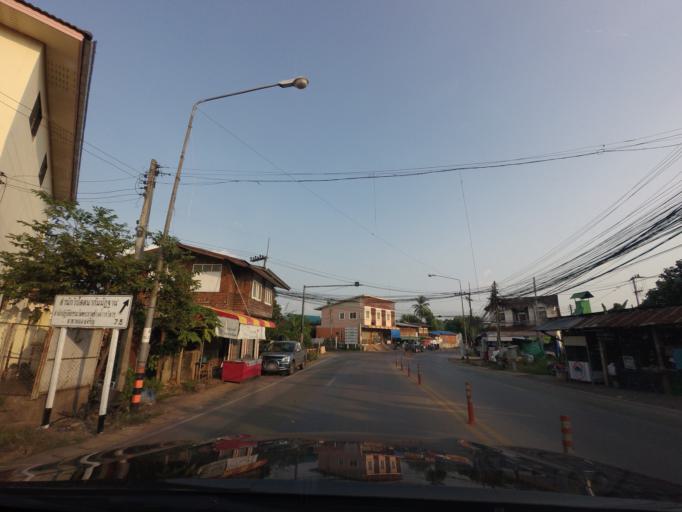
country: TH
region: Nan
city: Nan
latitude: 18.7737
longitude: 100.7807
